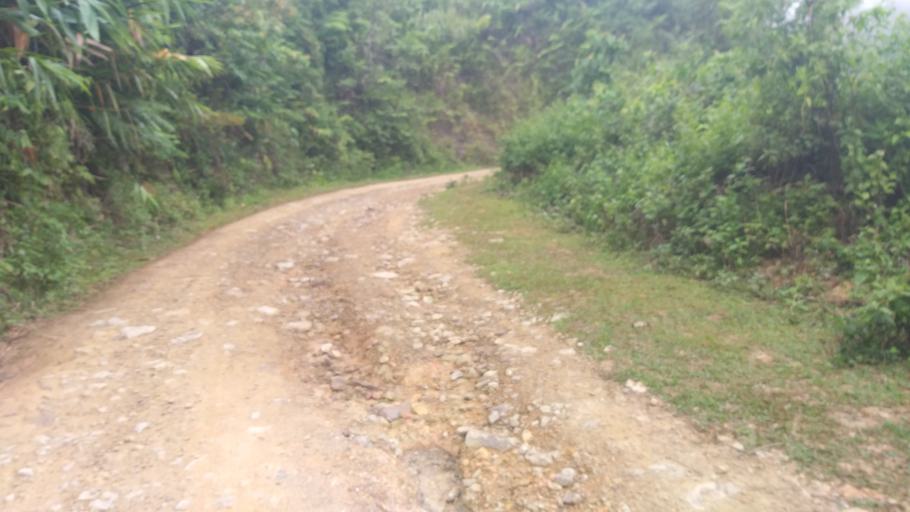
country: LA
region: Phongsali
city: Khoa
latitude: 21.2550
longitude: 102.6642
